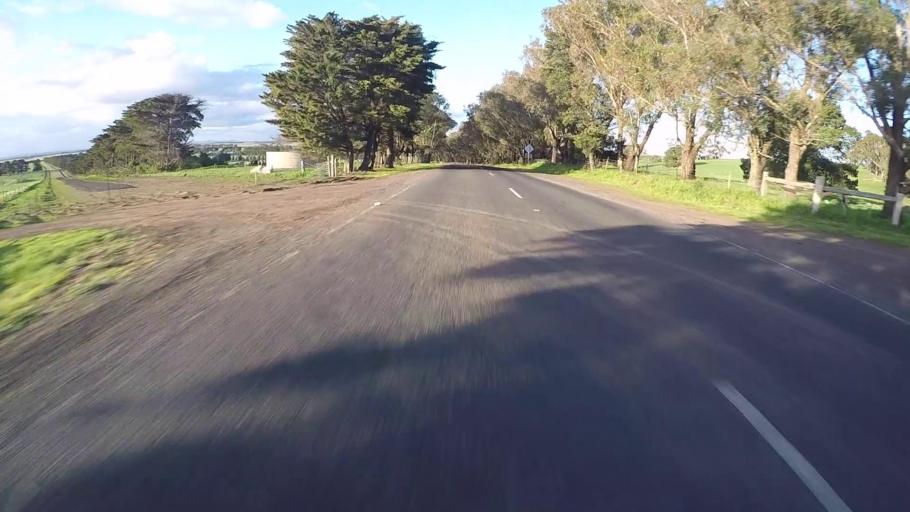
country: AU
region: Victoria
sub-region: Greater Geelong
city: Wandana Heights
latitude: -38.1514
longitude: 144.1756
